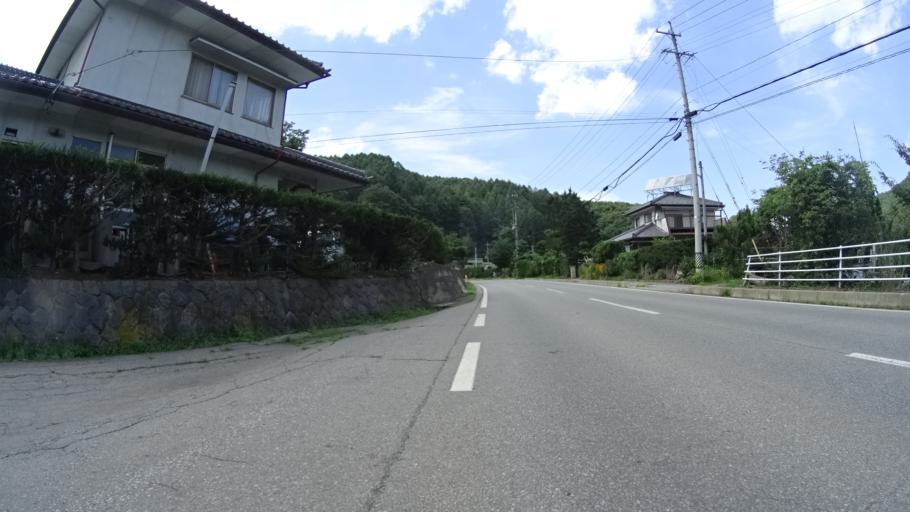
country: JP
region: Nagano
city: Saku
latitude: 36.0783
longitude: 138.4898
